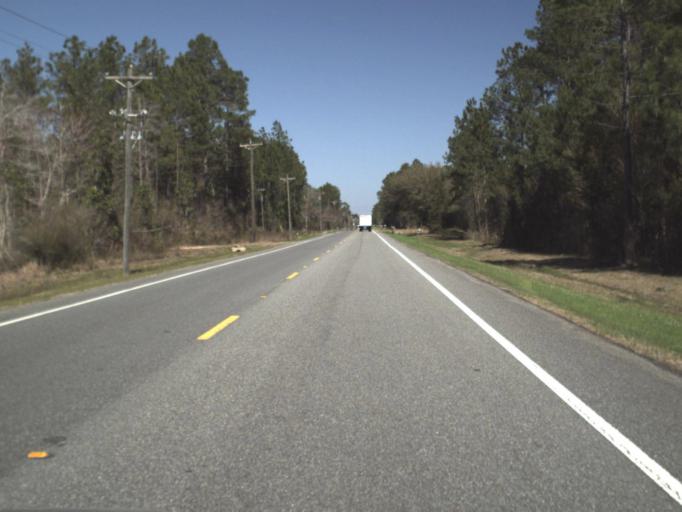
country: US
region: Florida
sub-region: Calhoun County
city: Blountstown
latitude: 30.4096
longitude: -85.0815
